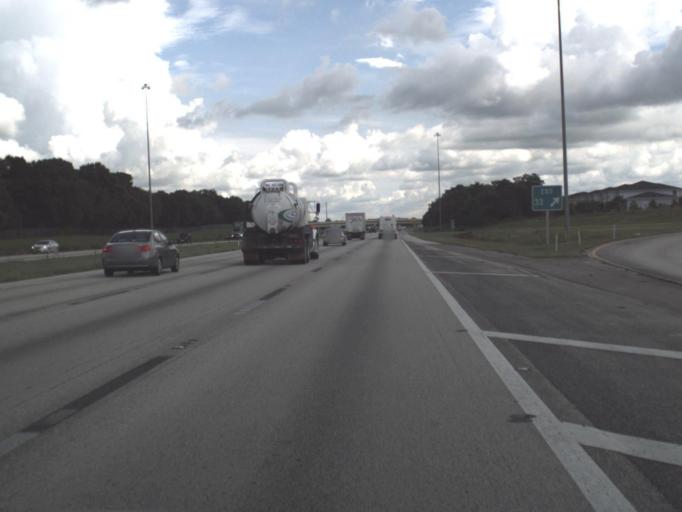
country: US
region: Florida
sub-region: Polk County
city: Gibsonia
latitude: 28.1041
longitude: -81.9464
